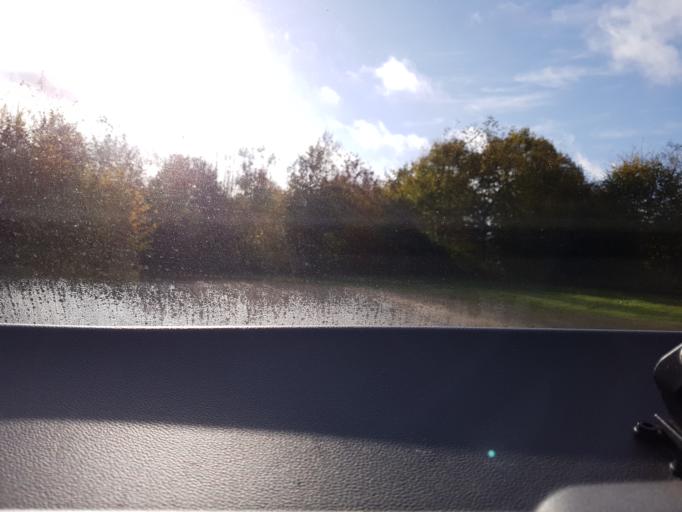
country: FR
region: Pays de la Loire
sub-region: Departement de la Mayenne
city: Ambrieres-les-Vallees
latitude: 48.3874
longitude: -0.5856
